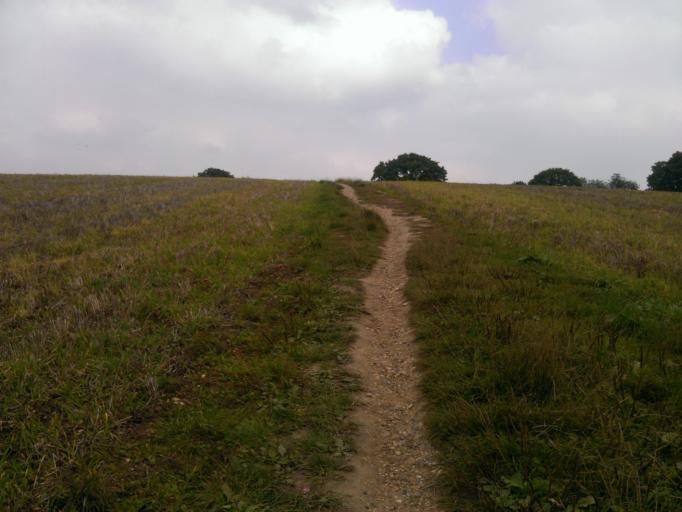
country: GB
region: England
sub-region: Essex
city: Rowhedge
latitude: 51.8698
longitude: 0.9531
